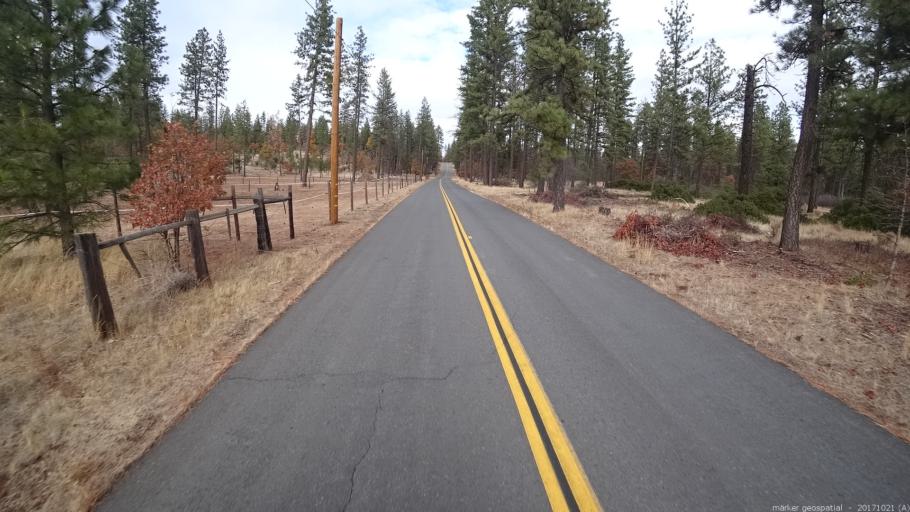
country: US
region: California
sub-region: Shasta County
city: Burney
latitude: 40.9430
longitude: -121.6456
